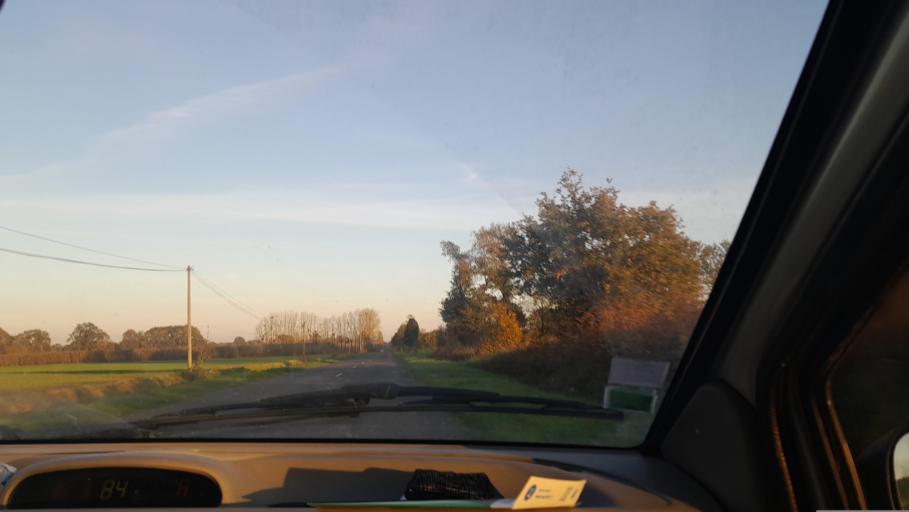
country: FR
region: Brittany
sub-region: Departement d'Ille-et-Vilaine
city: Le Pertre
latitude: 47.9673
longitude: -1.0691
